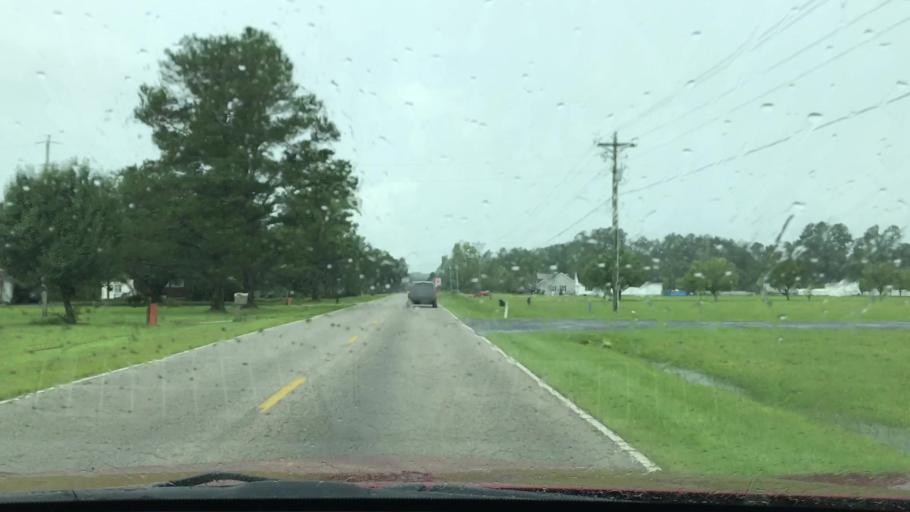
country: US
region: South Carolina
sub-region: Horry County
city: Red Hill
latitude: 33.8817
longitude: -78.9665
